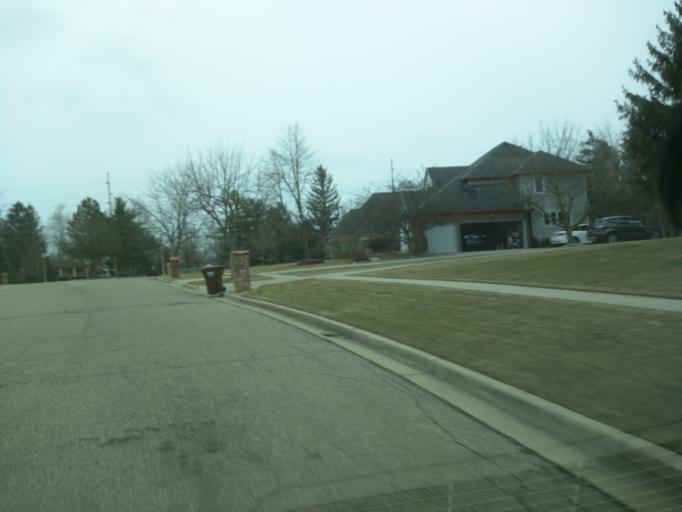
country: US
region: Michigan
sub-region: Eaton County
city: Waverly
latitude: 42.7566
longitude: -84.6353
